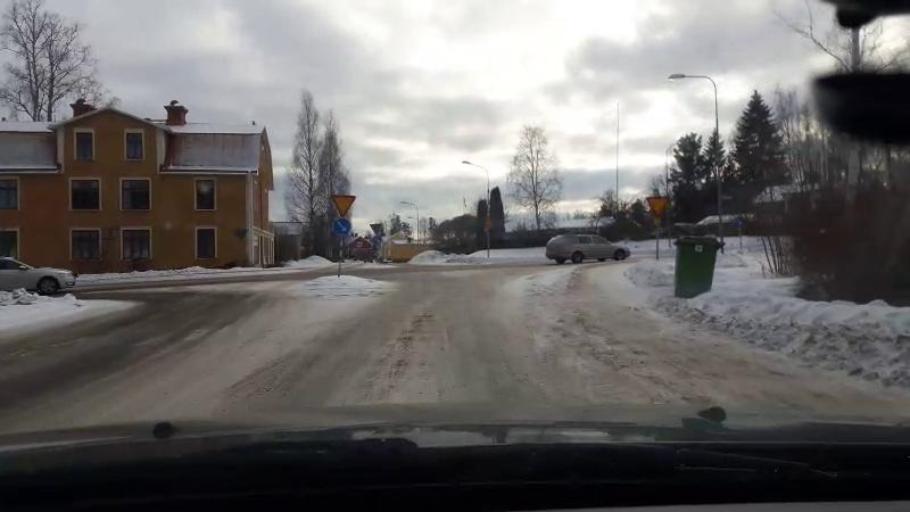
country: SE
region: Gaevleborg
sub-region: Bollnas Kommun
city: Bollnas
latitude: 61.3340
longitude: 16.3910
